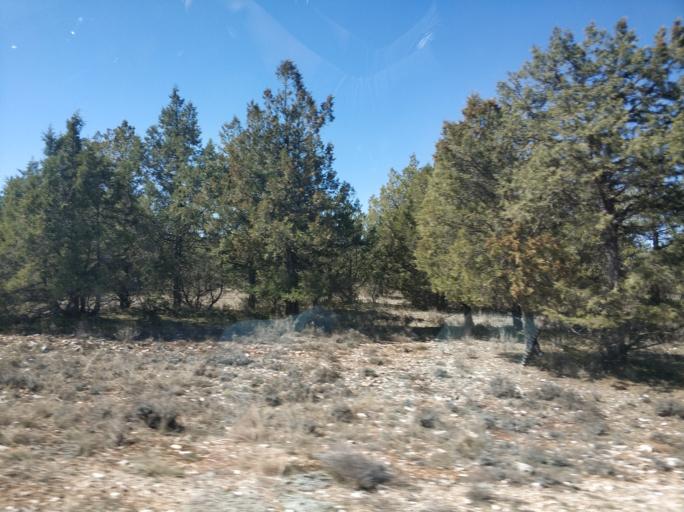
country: ES
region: Castille and Leon
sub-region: Provincia de Soria
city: Ucero
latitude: 41.7347
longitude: -3.0428
